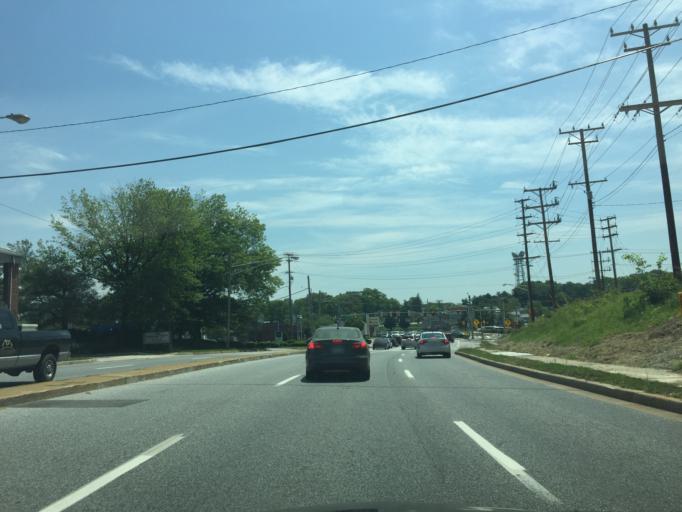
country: US
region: Maryland
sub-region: Baltimore County
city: Carney
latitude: 39.3954
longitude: -76.5247
